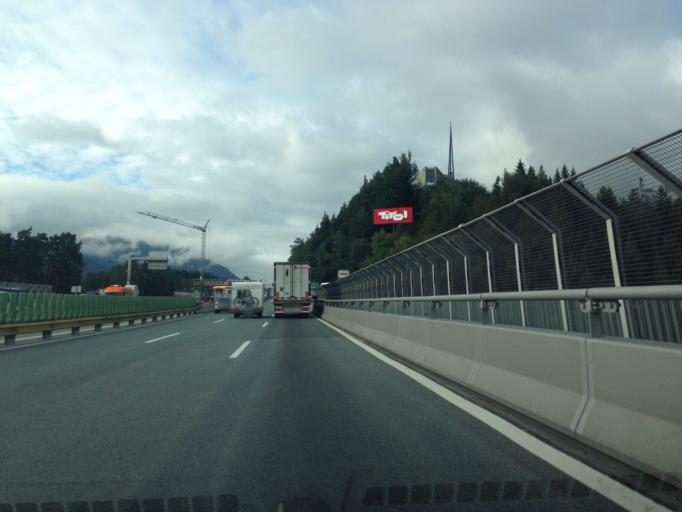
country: AT
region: Tyrol
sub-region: Politischer Bezirk Innsbruck Land
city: Patsch
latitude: 47.1998
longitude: 11.3998
